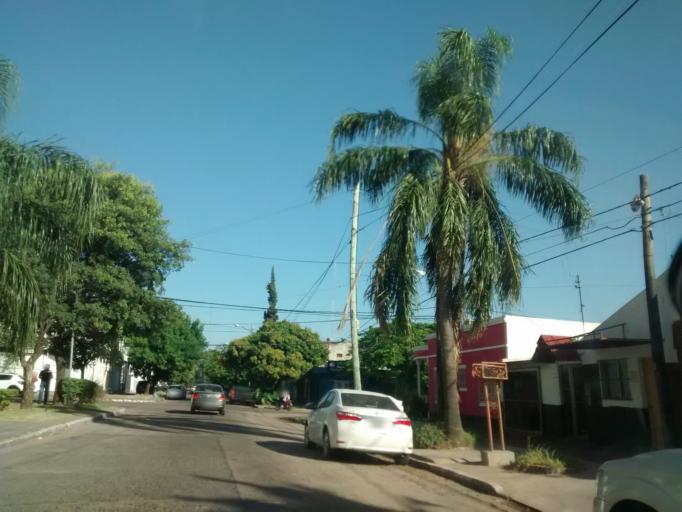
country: AR
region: Chaco
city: Resistencia
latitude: -27.4403
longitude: -58.9970
